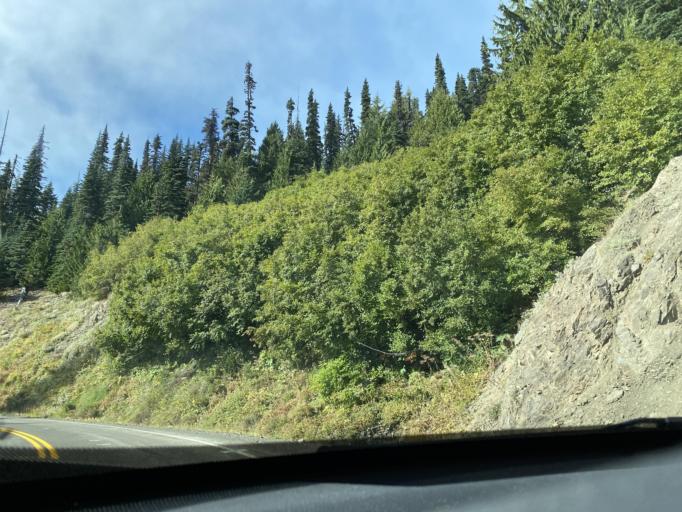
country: US
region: Washington
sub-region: Clallam County
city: Port Angeles
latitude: 47.9826
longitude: -123.4677
